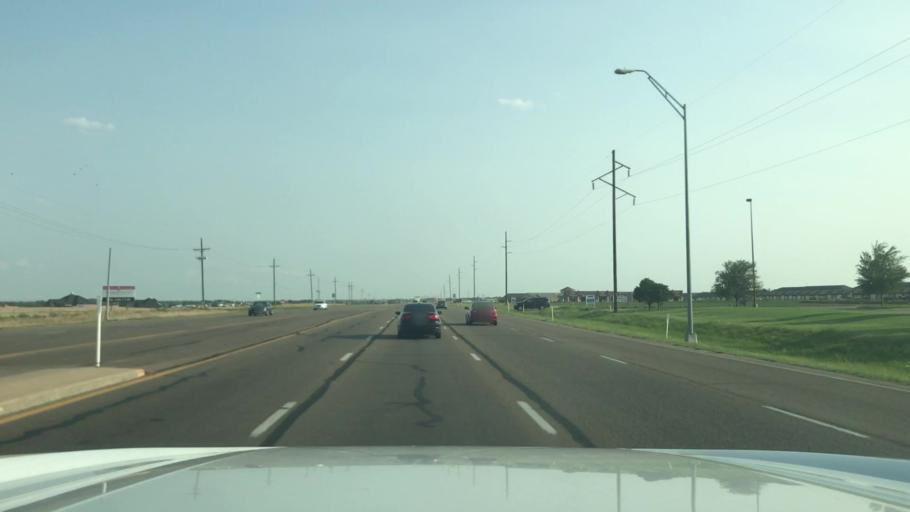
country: US
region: Texas
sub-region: Potter County
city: Amarillo
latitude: 35.1452
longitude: -101.9382
